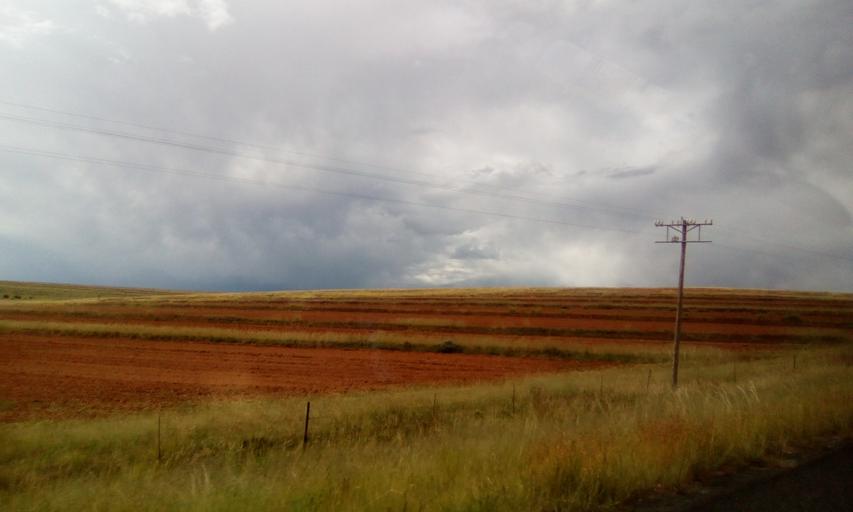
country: ZA
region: Orange Free State
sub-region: Thabo Mofutsanyana District Municipality
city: Ladybrand
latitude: -29.2271
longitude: 27.4521
